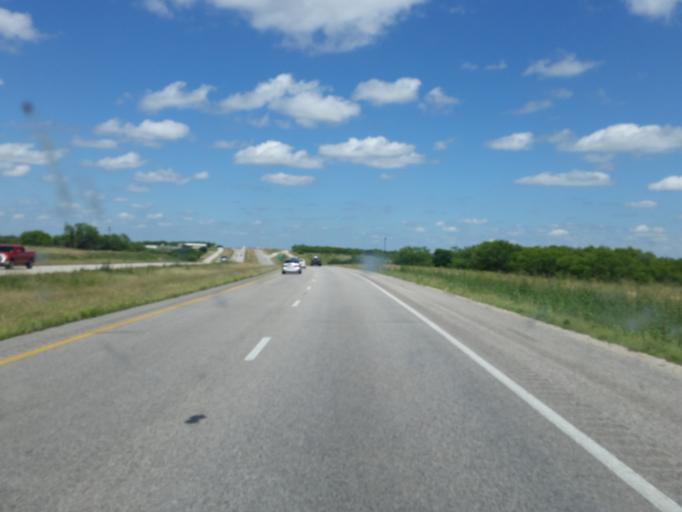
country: US
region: Texas
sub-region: Eastland County
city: Cisco
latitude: 32.3722
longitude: -99.1865
